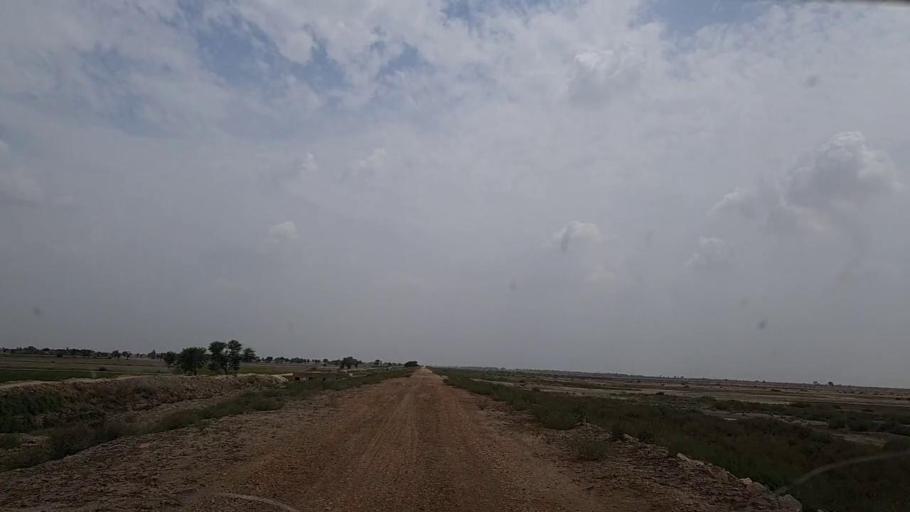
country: PK
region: Sindh
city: Johi
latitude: 26.7869
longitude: 67.5995
